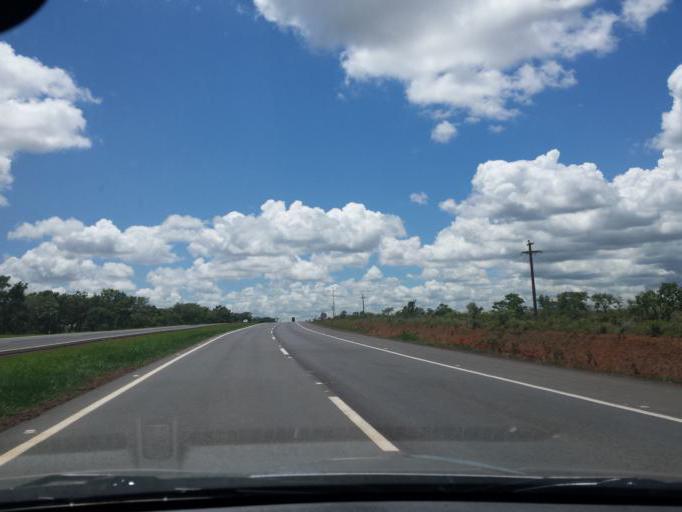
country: BR
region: Goias
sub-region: Cristalina
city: Cristalina
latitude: -16.6698
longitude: -47.7131
